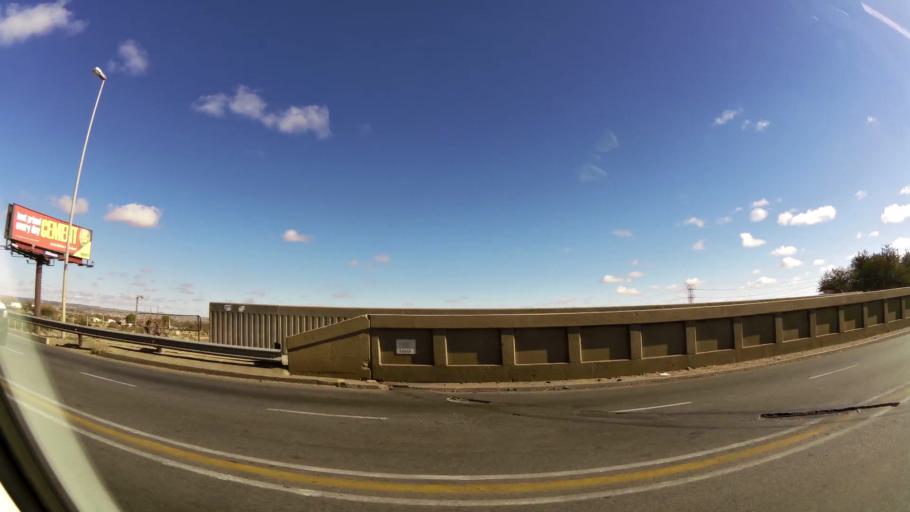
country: ZA
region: Limpopo
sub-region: Capricorn District Municipality
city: Polokwane
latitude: -23.8796
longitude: 29.4600
